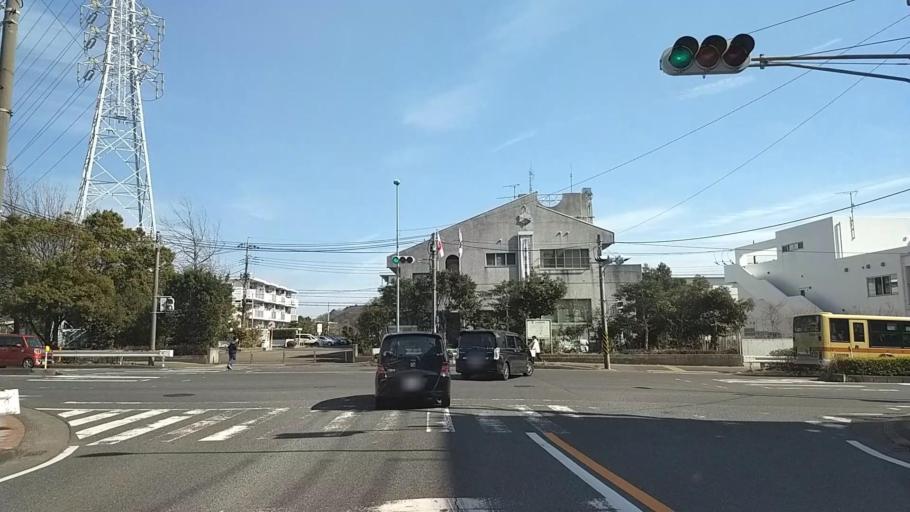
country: JP
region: Kanagawa
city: Fujisawa
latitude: 35.3638
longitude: 139.4452
